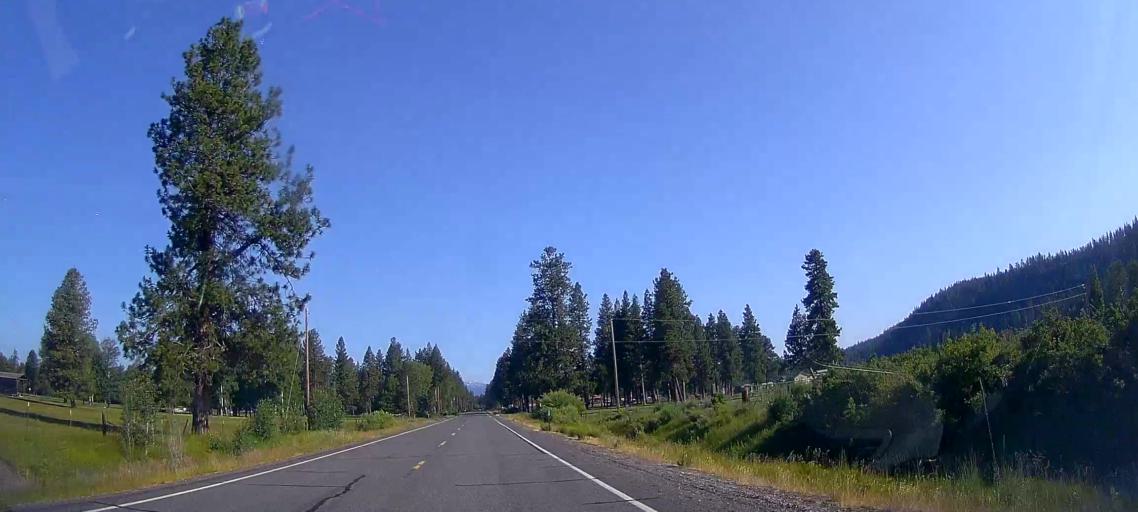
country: US
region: Oregon
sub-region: Klamath County
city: Klamath Falls
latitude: 42.6728
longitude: -121.9689
